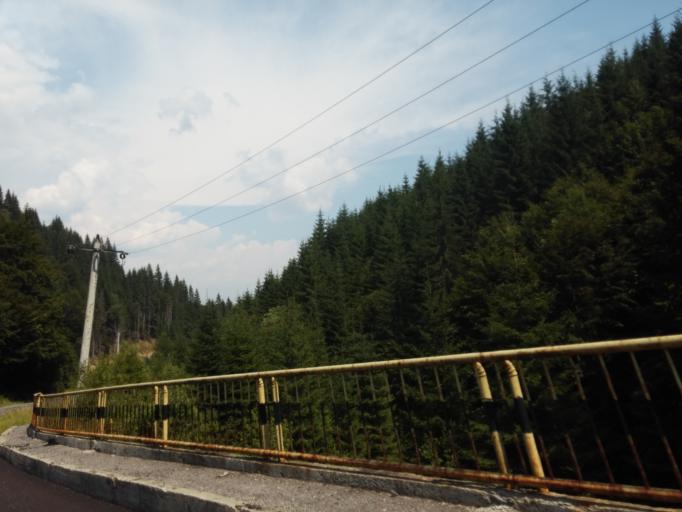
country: RO
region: Valcea
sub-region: Comuna Voineasa
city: Voineasa
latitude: 45.4307
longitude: 23.8370
